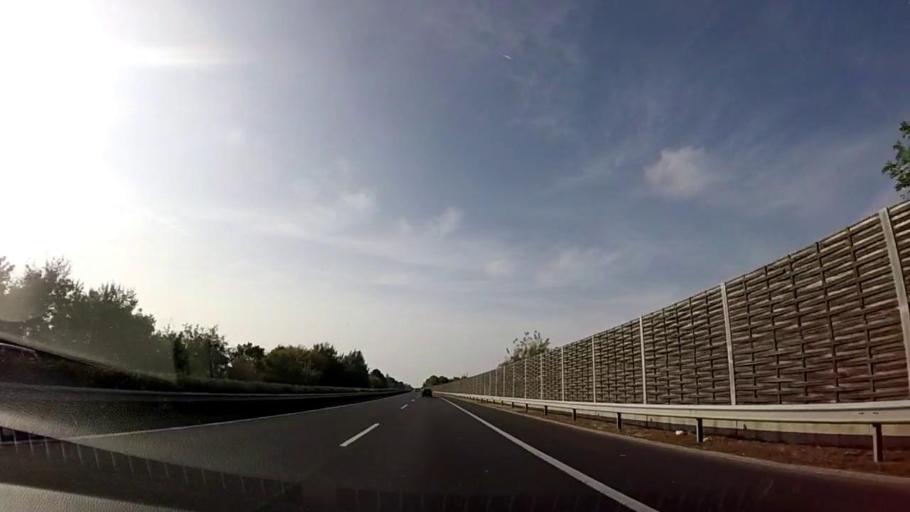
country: HU
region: Fejer
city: Lepseny
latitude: 46.9815
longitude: 18.1764
